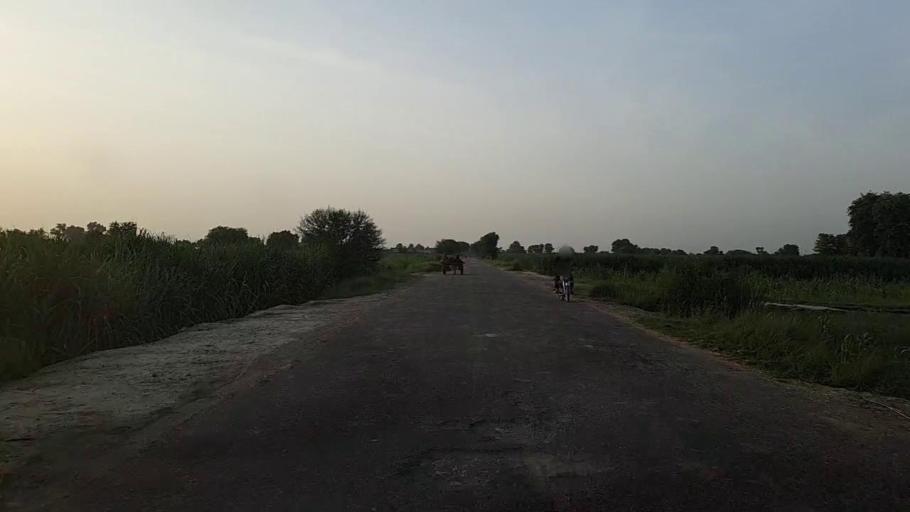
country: PK
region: Sindh
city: Ubauro
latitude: 28.2267
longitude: 69.8178
